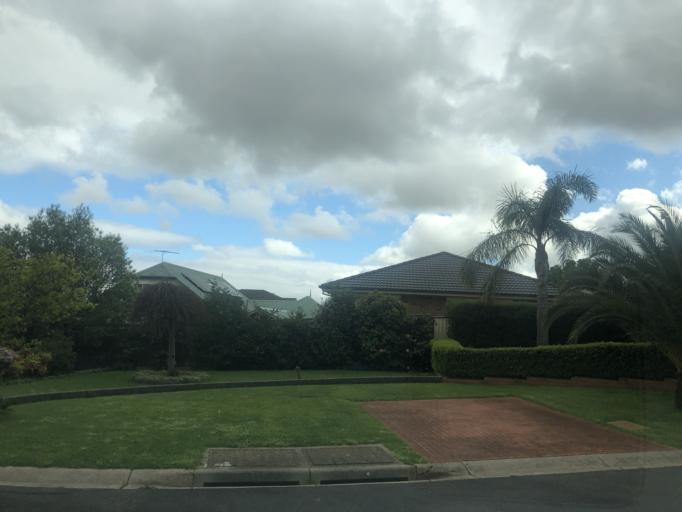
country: AU
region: Victoria
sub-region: Knox
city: Rowville
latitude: -37.9374
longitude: 145.2534
